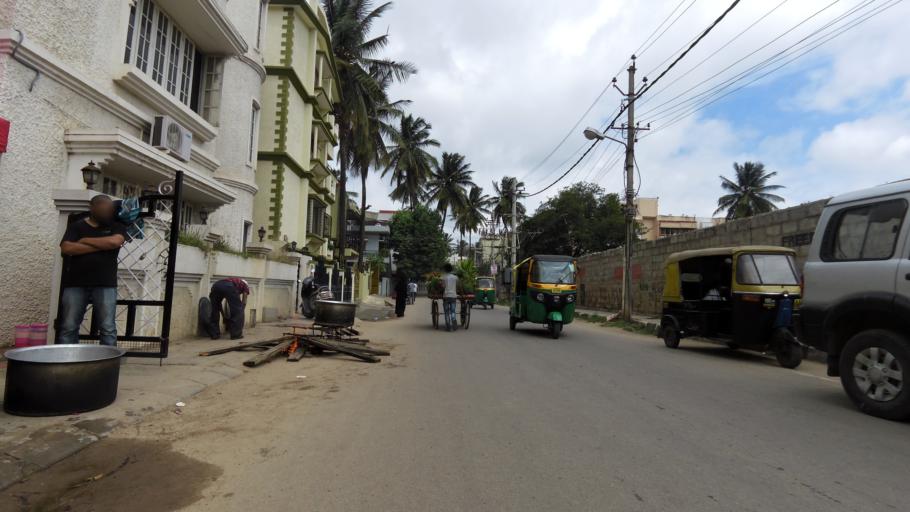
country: IN
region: Karnataka
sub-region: Bangalore Urban
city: Bangalore
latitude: 13.0059
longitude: 77.6265
